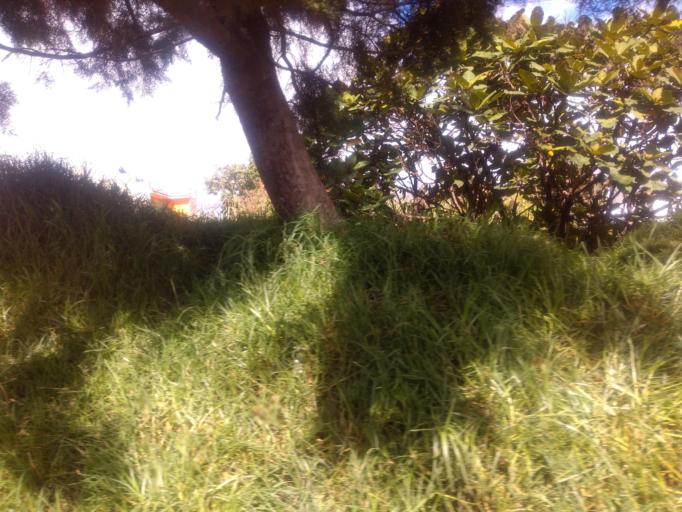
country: GT
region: Quetzaltenango
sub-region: Municipio de La Esperanza
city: La Esperanza
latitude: 14.8613
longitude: -91.5656
